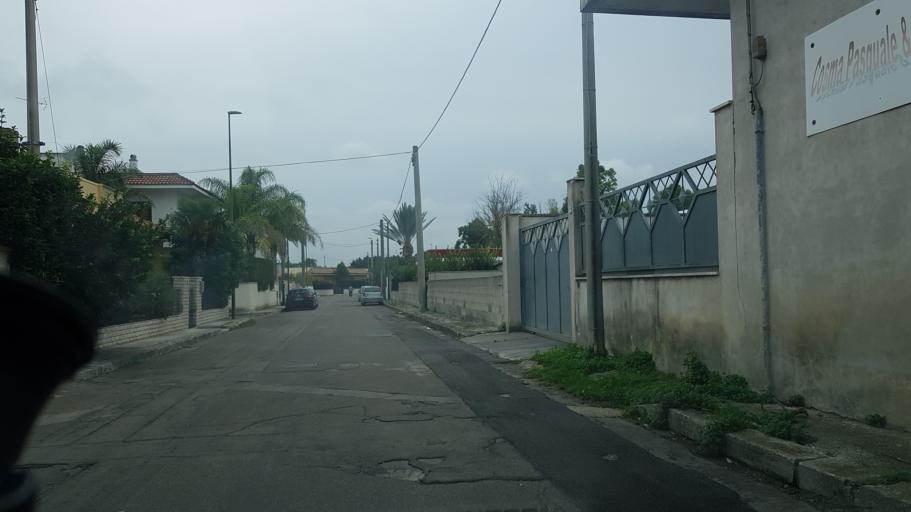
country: IT
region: Apulia
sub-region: Provincia di Lecce
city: Guagnano
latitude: 40.3995
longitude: 17.9449
